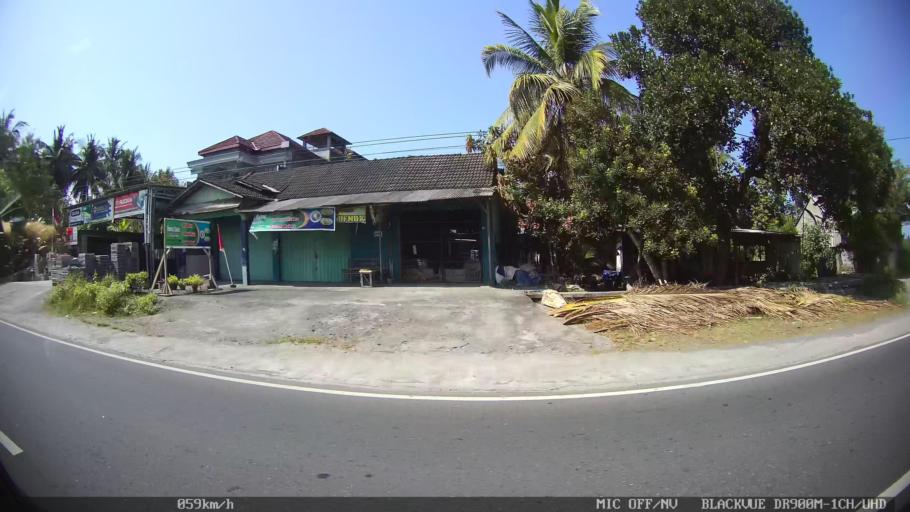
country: ID
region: Daerah Istimewa Yogyakarta
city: Srandakan
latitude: -7.9300
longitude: 110.1963
